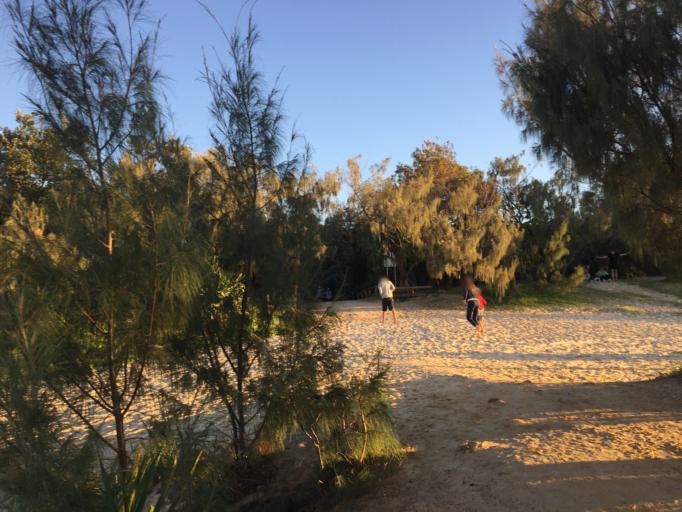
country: AU
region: Queensland
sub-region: Sunshine Coast
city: Noosa Heads
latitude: -26.3846
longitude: 153.0865
